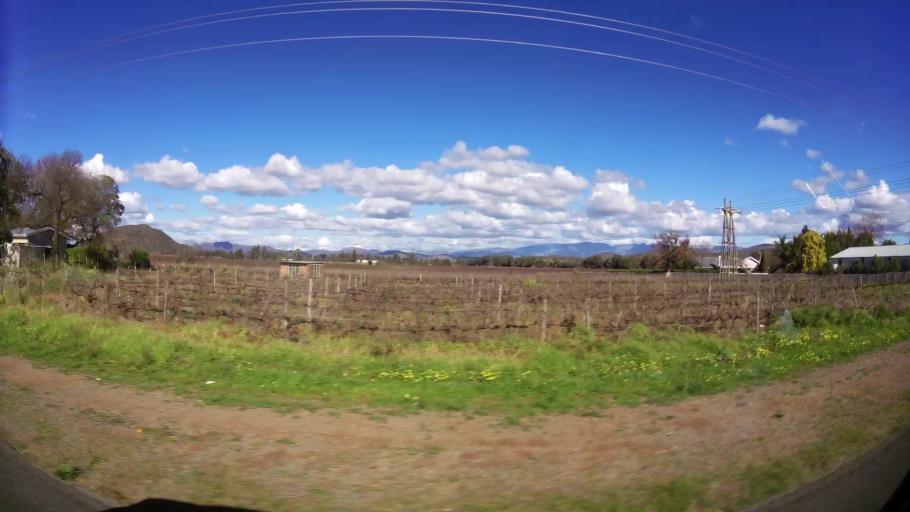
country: ZA
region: Western Cape
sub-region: Cape Winelands District Municipality
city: Ashton
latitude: -33.8072
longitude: 19.8610
